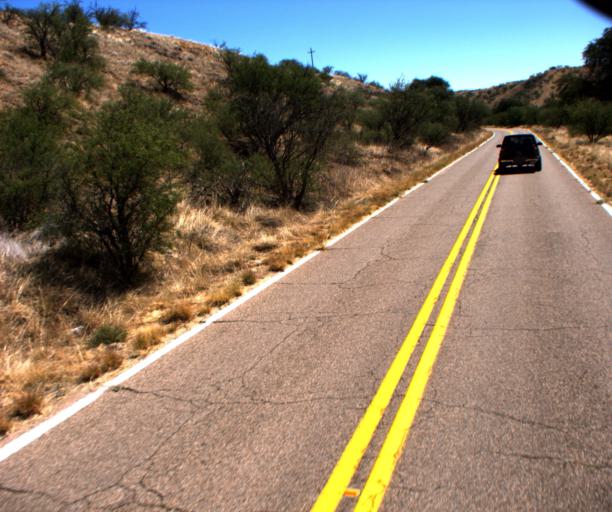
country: US
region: Arizona
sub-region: Santa Cruz County
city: Rio Rico
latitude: 31.3973
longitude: -111.0343
